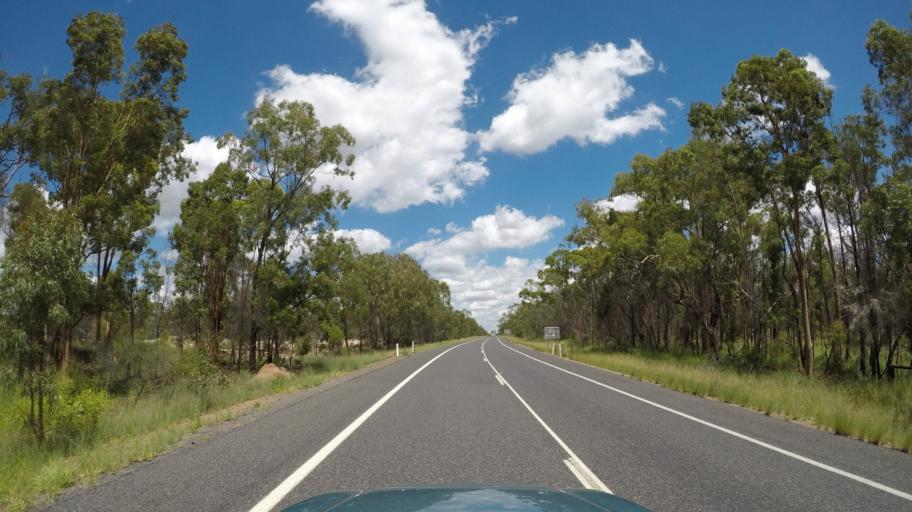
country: AU
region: Queensland
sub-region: Western Downs
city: Dalby
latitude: -27.9774
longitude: 151.0889
